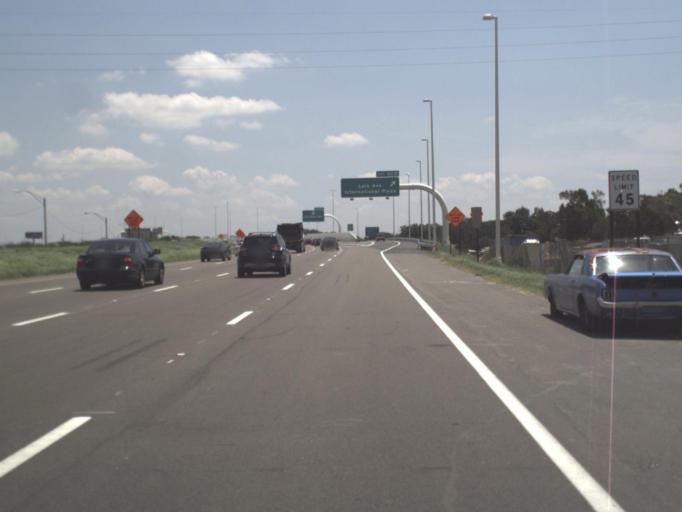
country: US
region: Florida
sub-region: Hillsborough County
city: Tampa
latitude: 27.9502
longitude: -82.5194
